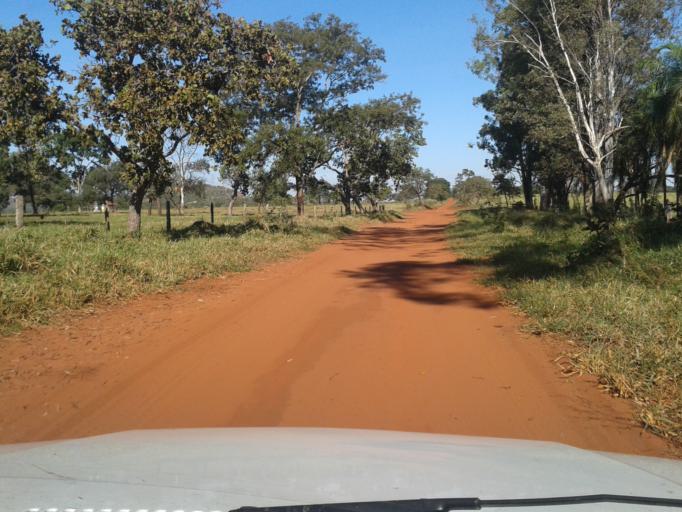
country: BR
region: Minas Gerais
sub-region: Ituiutaba
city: Ituiutaba
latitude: -19.0980
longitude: -49.8101
